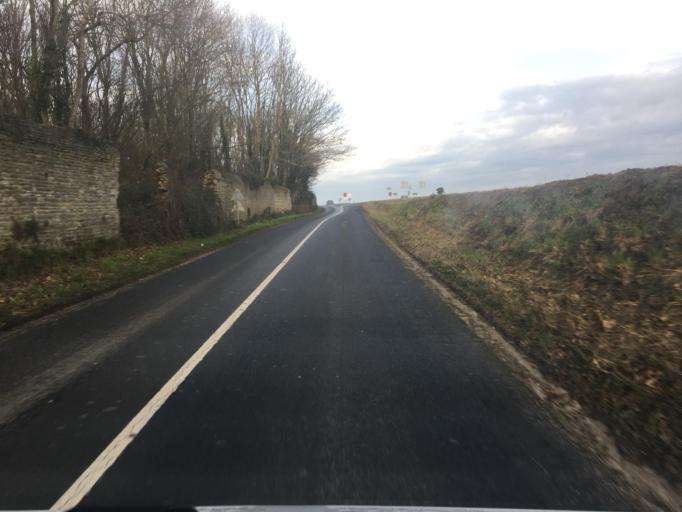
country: FR
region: Lower Normandy
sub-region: Departement du Calvados
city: Creully
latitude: 49.2922
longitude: -0.5429
